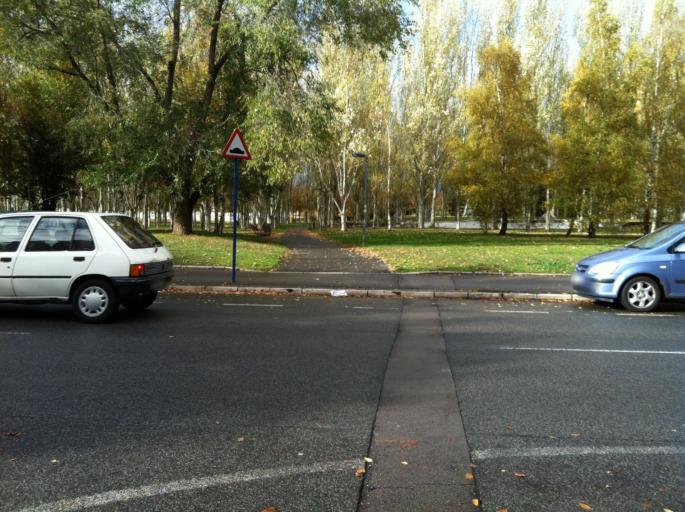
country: ES
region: Basque Country
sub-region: Provincia de Alava
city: Gasteiz / Vitoria
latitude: 42.8580
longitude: -2.6996
